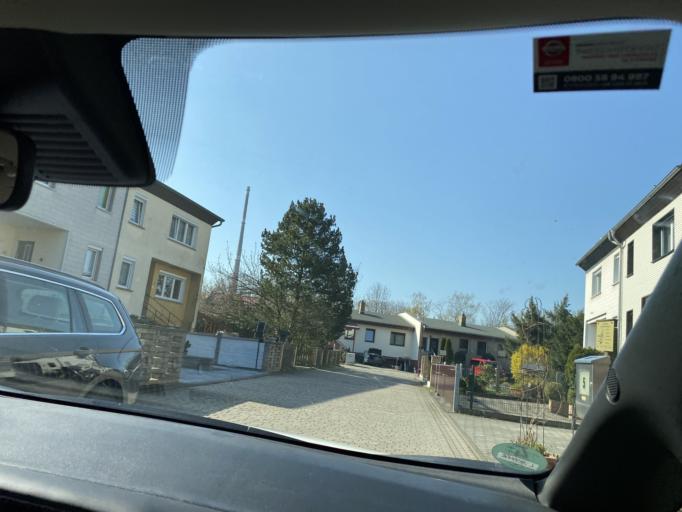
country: DE
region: Saxony
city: Kitzen
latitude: 51.2527
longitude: 12.2695
